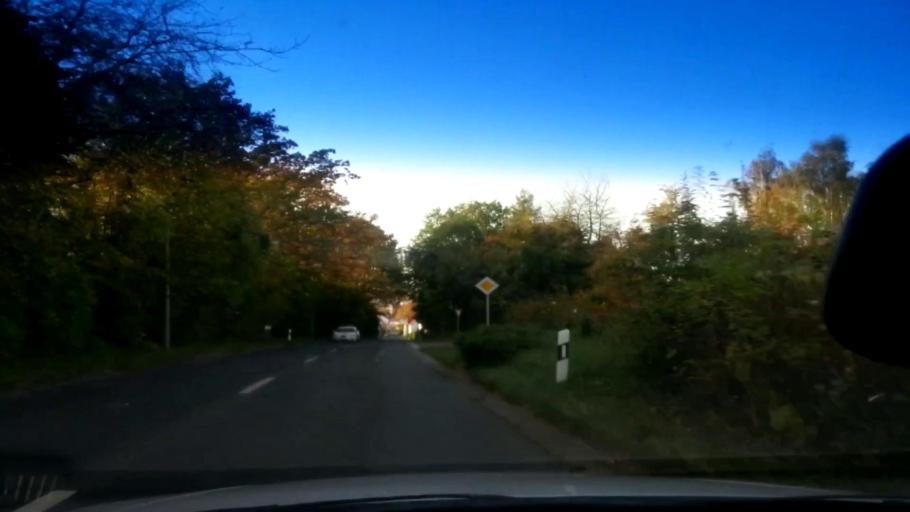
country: DE
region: Bavaria
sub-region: Upper Franconia
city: Schesslitz
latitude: 49.9718
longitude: 11.0421
